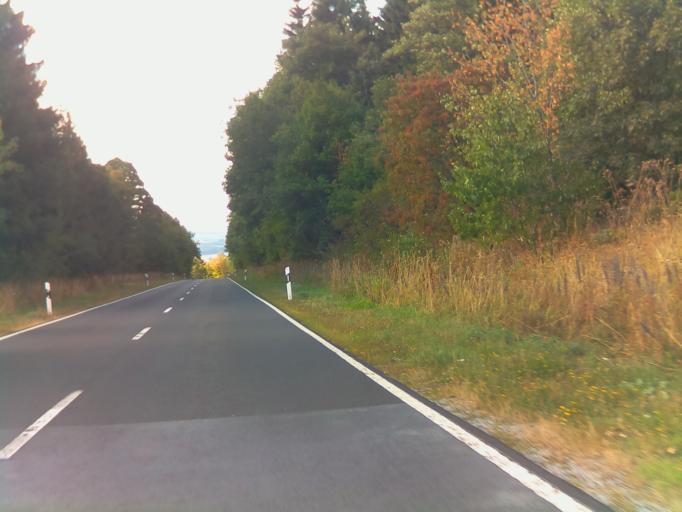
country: DE
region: Thuringia
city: Birx
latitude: 50.5104
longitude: 10.0405
